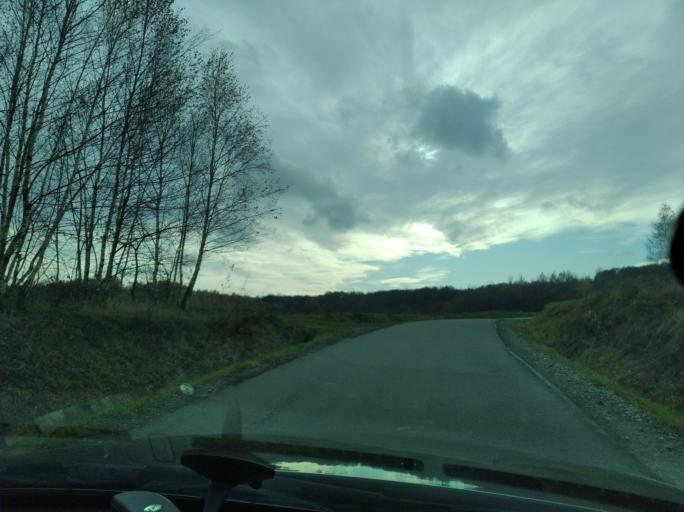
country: PL
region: Subcarpathian Voivodeship
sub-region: Powiat strzyzowski
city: Strzyzow
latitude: 49.9241
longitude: 21.7720
